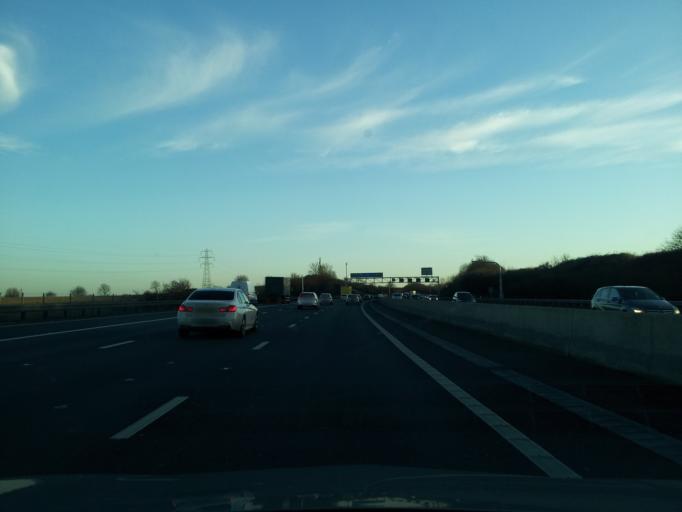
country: GB
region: England
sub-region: Central Bedfordshire
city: Steppingley
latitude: 51.9816
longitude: -0.5272
